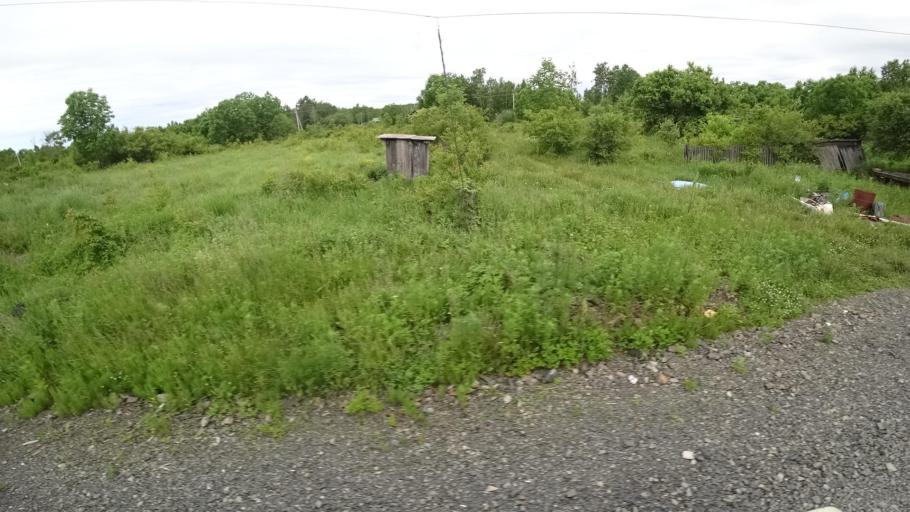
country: RU
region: Khabarovsk Krai
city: Amursk
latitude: 49.8898
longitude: 136.1296
